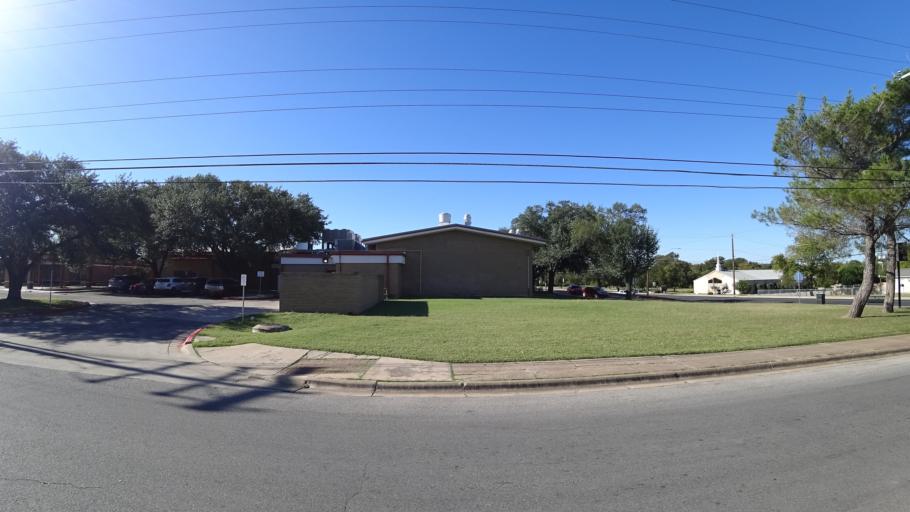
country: US
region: Texas
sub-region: Travis County
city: Austin
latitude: 30.2792
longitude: -97.6735
